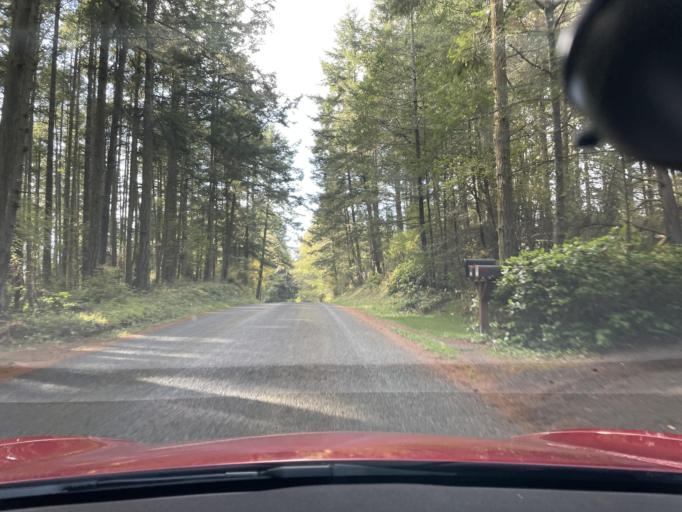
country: US
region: Washington
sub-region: San Juan County
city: Friday Harbor
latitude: 48.4818
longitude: -123.0406
